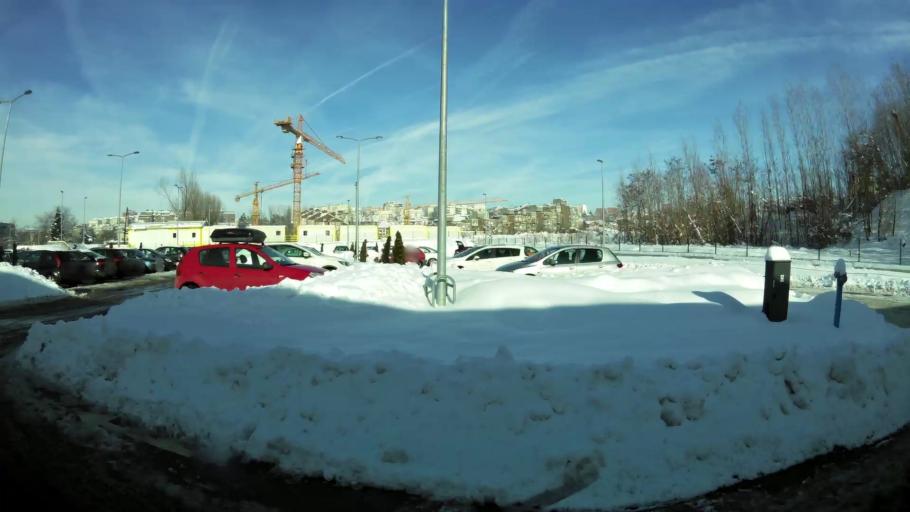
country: RS
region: Central Serbia
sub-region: Belgrade
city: Vozdovac
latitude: 44.7850
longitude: 20.5019
